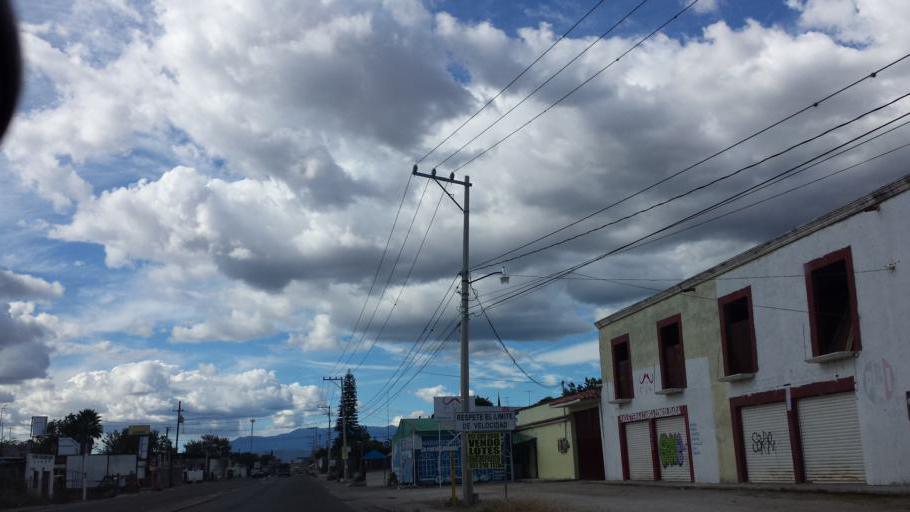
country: MX
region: Oaxaca
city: Tlacolula de Matamoros
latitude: 16.9530
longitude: -96.4687
